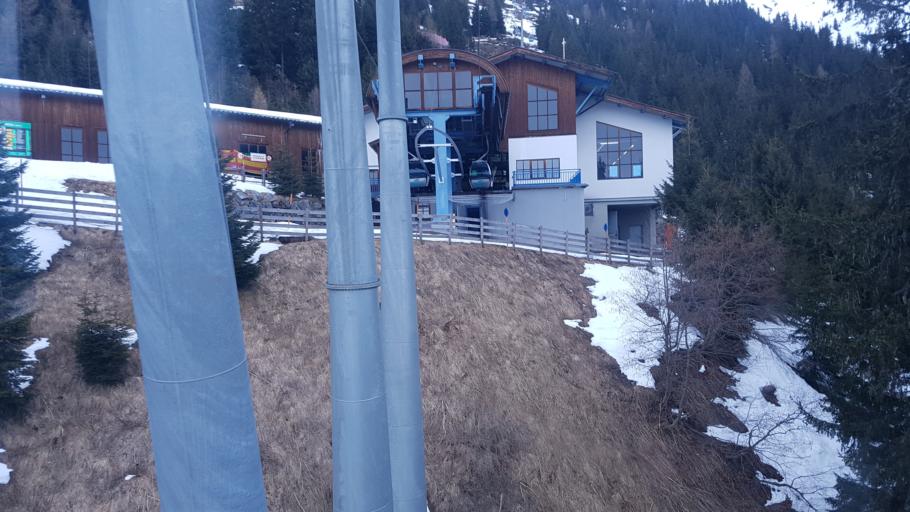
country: AT
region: Salzburg
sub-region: Politischer Bezirk Zell am See
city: Neukirchen am Grossvenediger
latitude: 47.2701
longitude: 12.2808
